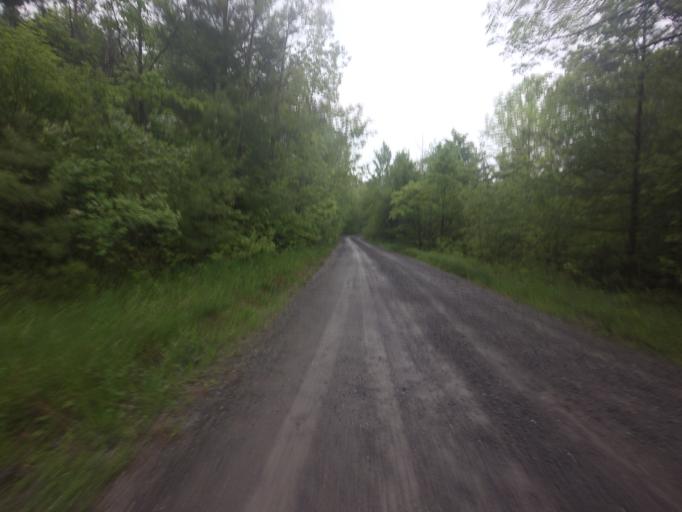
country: CA
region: Ontario
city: Kingston
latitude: 44.4522
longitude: -76.6033
